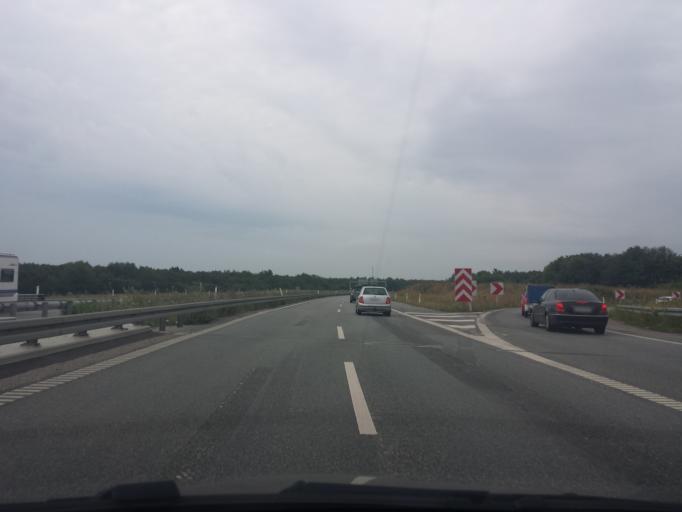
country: DK
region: Capital Region
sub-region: Ballerup Kommune
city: Ballerup
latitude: 55.7027
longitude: 12.3670
